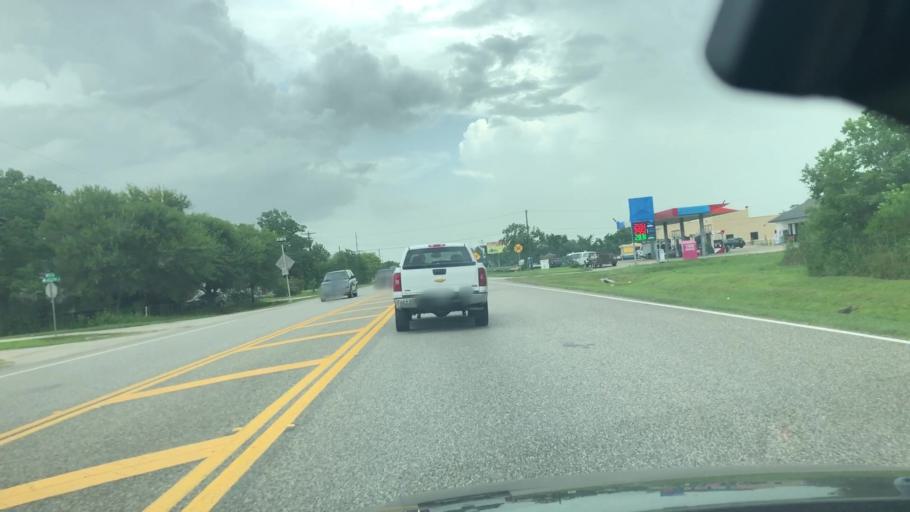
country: US
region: Texas
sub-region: Galveston County
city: Dickinson
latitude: 29.4813
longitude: -95.0686
